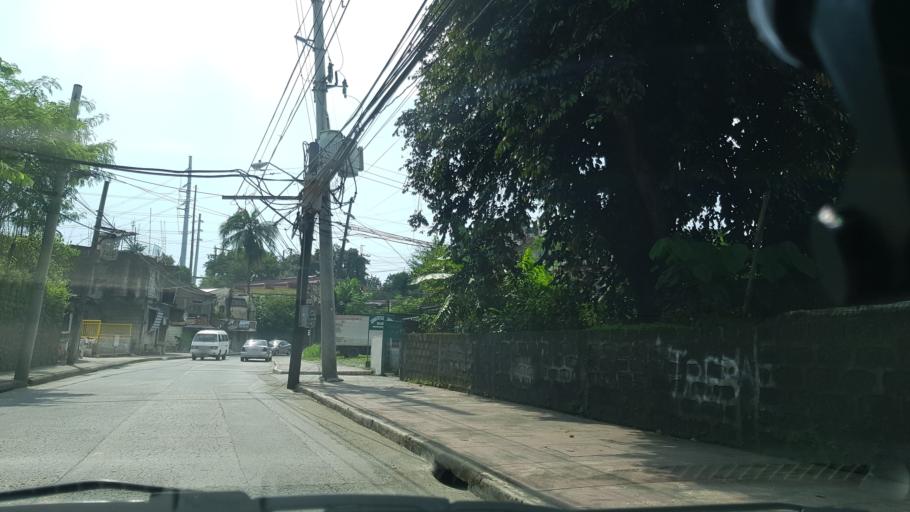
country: PH
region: Calabarzon
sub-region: Province of Rizal
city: Antipolo
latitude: 14.6582
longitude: 121.1278
